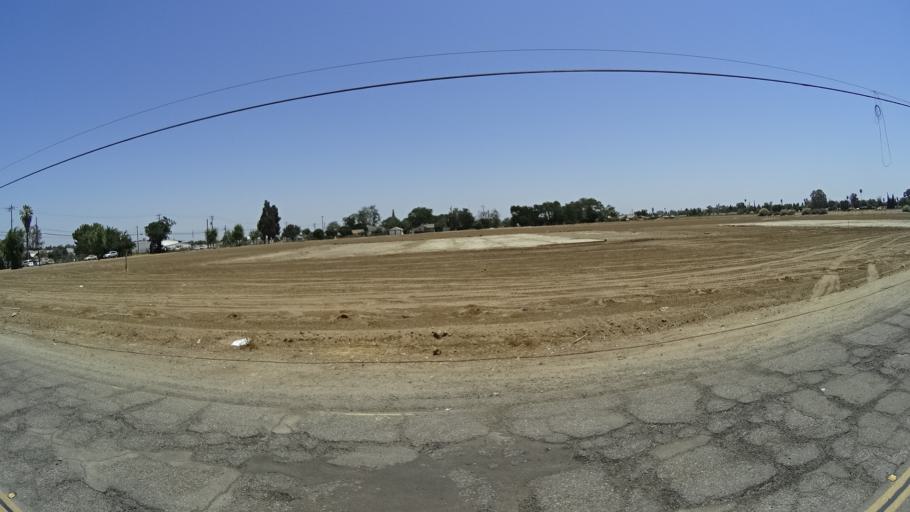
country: US
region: California
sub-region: Fresno County
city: West Park
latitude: 36.7350
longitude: -119.8357
